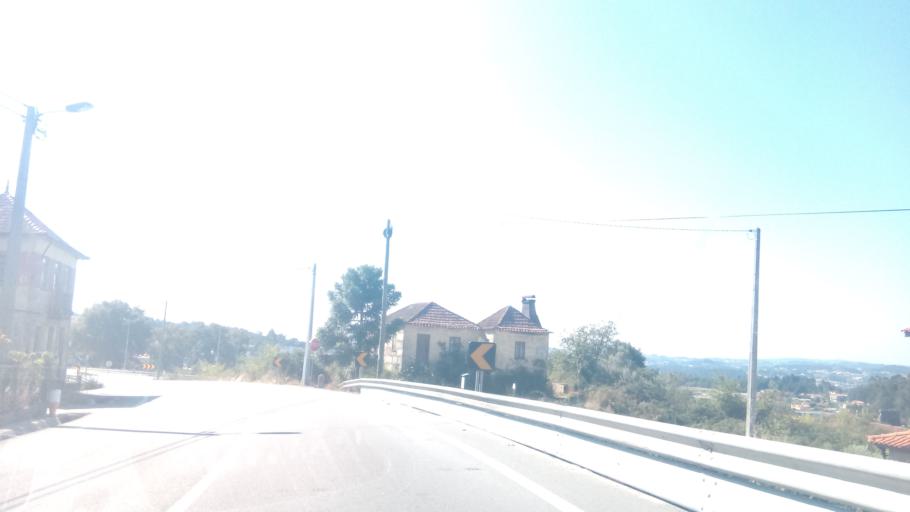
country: PT
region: Porto
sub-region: Amarante
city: Figueiro
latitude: 41.2868
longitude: -8.1990
